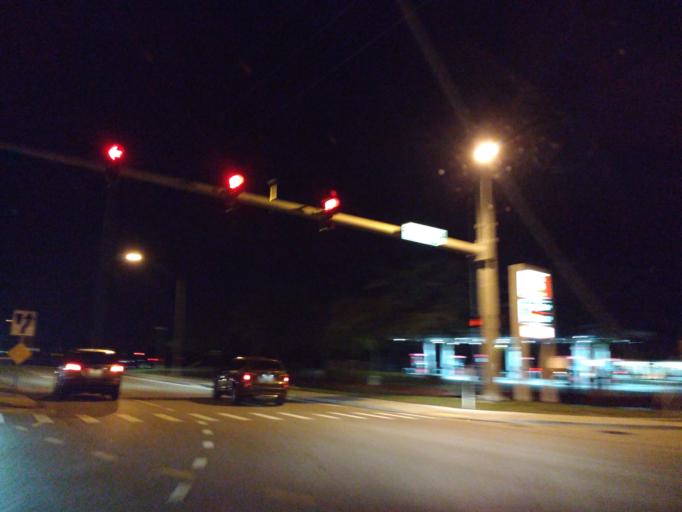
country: US
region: Florida
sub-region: Lee County
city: Lochmoor Waterway Estates
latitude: 26.6324
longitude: -81.9743
